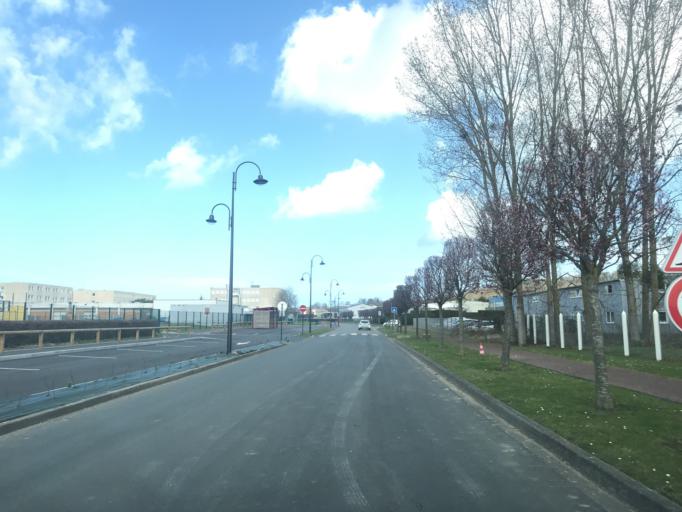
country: FR
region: Lower Normandy
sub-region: Departement du Calvados
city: Dives-sur-Mer
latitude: 49.2773
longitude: -0.0954
